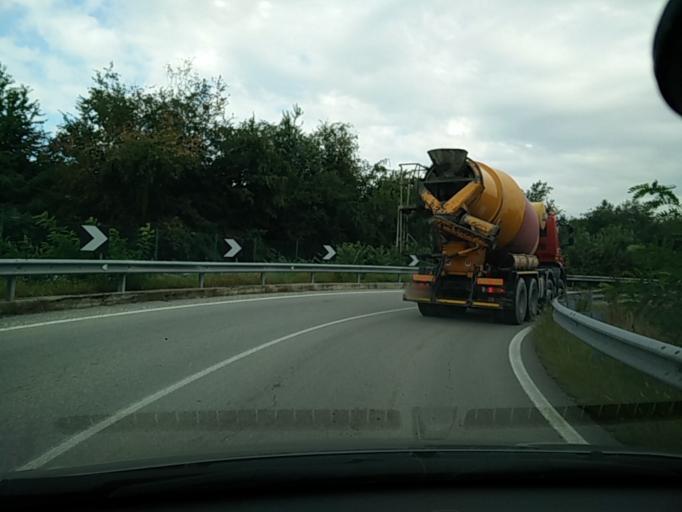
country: IT
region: Lombardy
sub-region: Provincia di Varese
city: Vizzola Ticino
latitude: 45.6496
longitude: 8.7131
